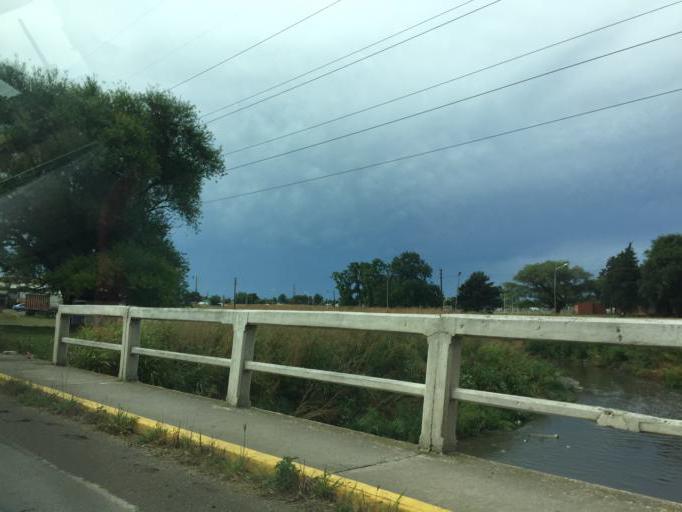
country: AR
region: Buenos Aires
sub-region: Partido de Tandil
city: Tandil
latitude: -37.2988
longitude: -59.1304
